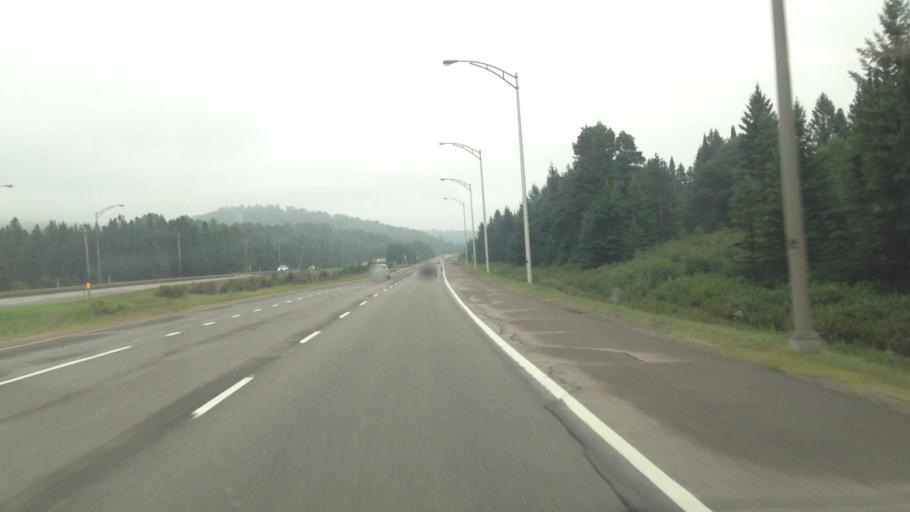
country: CA
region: Quebec
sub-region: Laurentides
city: Sainte-Agathe-des-Monts
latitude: 46.0973
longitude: -74.3561
